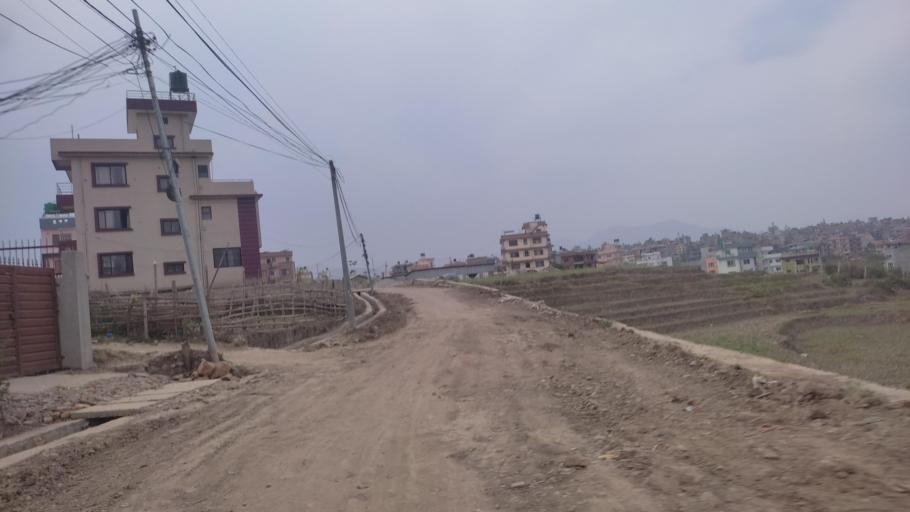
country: NP
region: Central Region
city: Kirtipur
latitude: 27.6628
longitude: 85.2776
